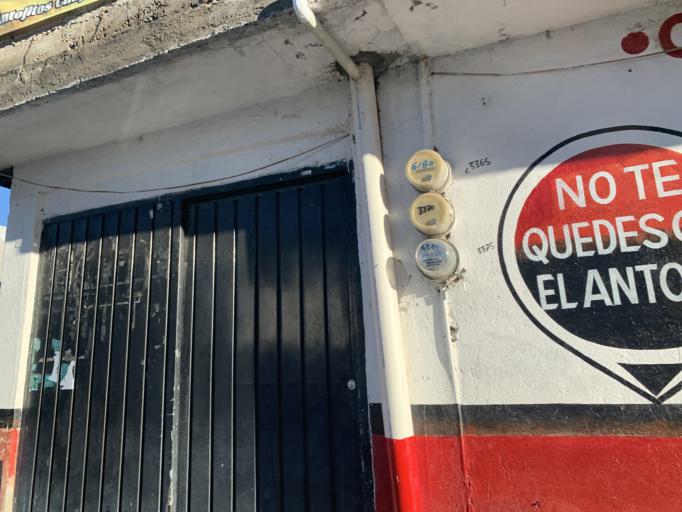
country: MX
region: Puebla
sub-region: Cuautlancingo
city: La Trinidad Chautenco
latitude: 19.0833
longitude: -98.2505
